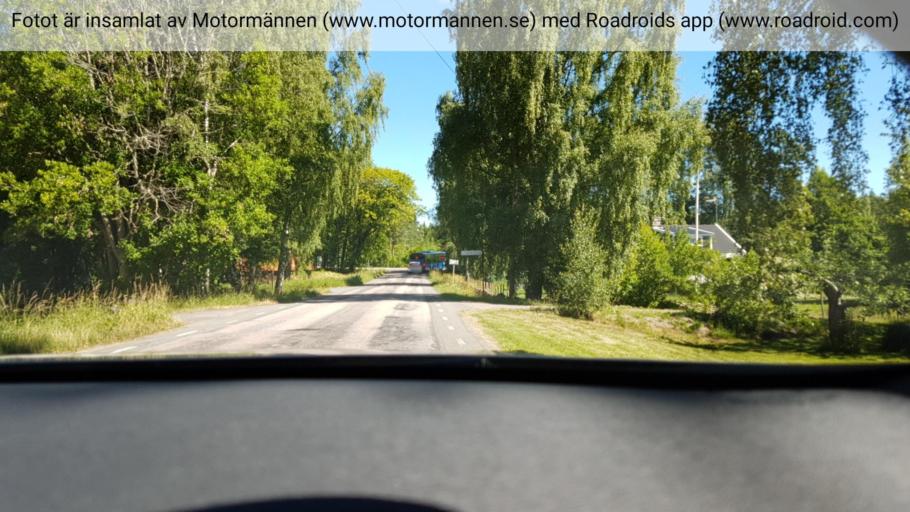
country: SE
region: Vaestra Goetaland
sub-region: Tidaholms Kommun
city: Tidaholm
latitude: 58.2153
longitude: 13.8566
